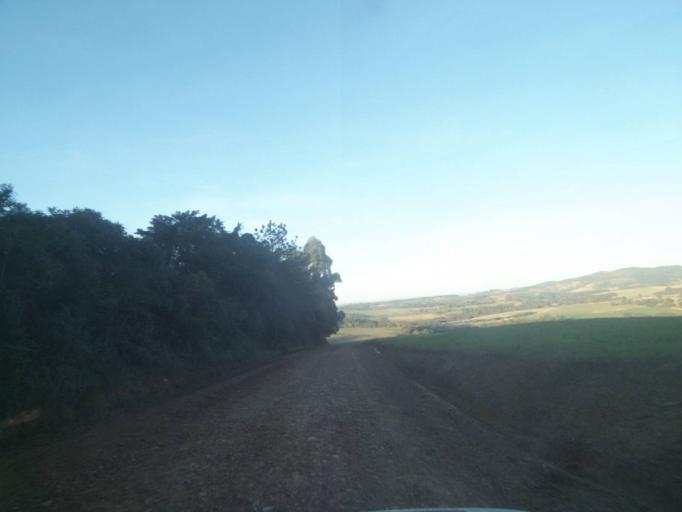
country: BR
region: Parana
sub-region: Tibagi
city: Tibagi
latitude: -24.5358
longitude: -50.5256
